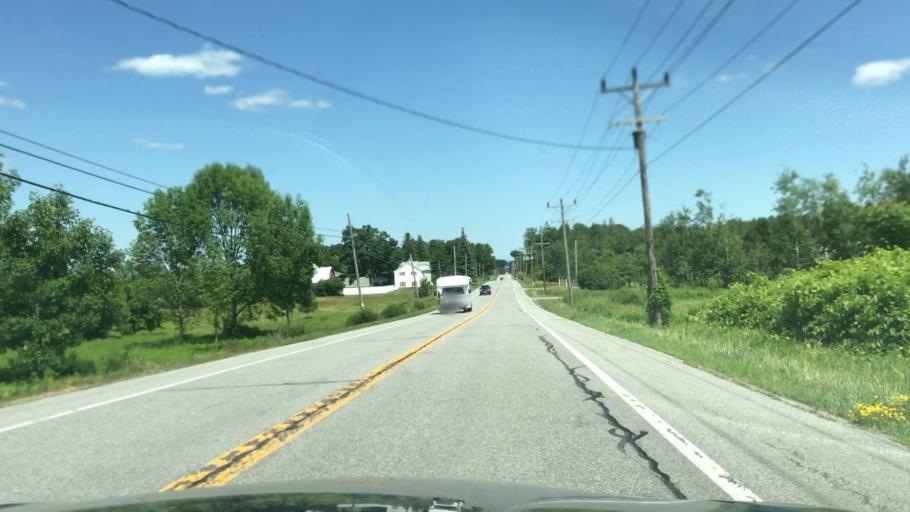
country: US
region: New York
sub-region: Wyoming County
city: Perry
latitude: 42.7444
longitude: -78.0565
